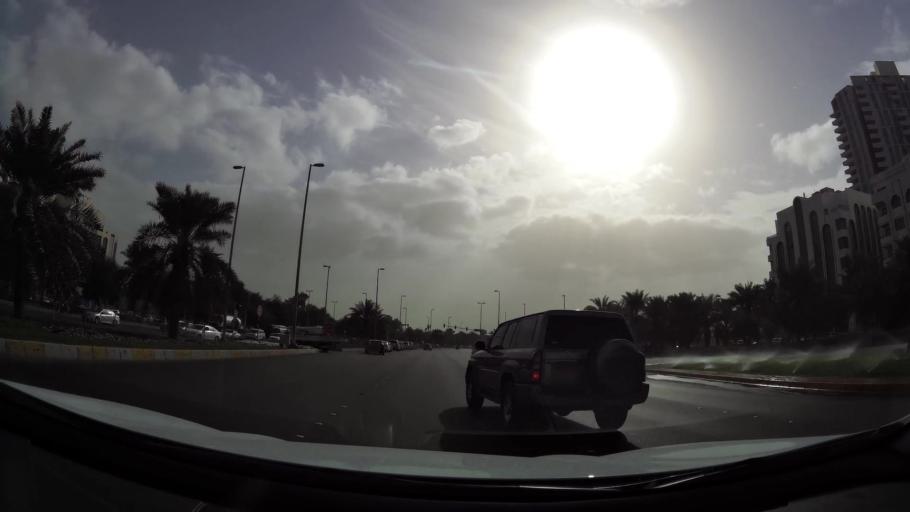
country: AE
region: Abu Dhabi
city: Abu Dhabi
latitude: 24.4329
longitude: 54.4372
